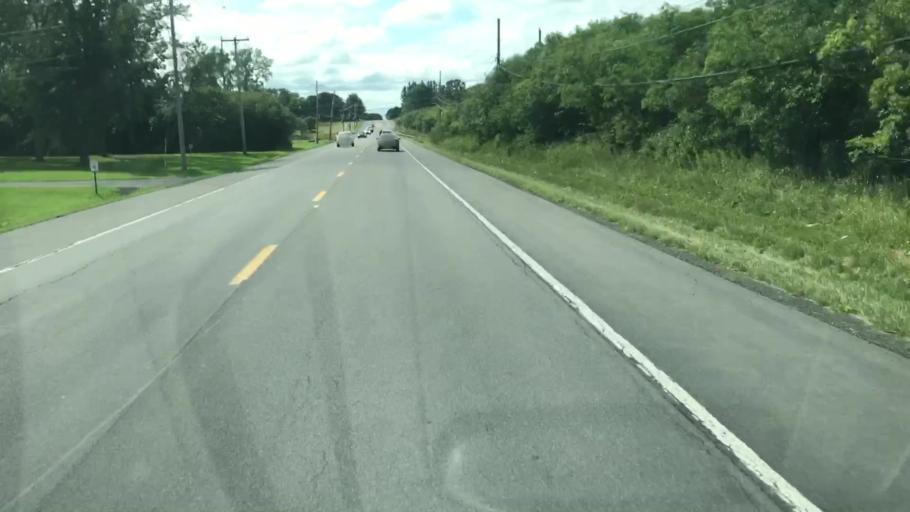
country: US
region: New York
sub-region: Cayuga County
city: Melrose Park
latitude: 42.9372
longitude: -76.5179
